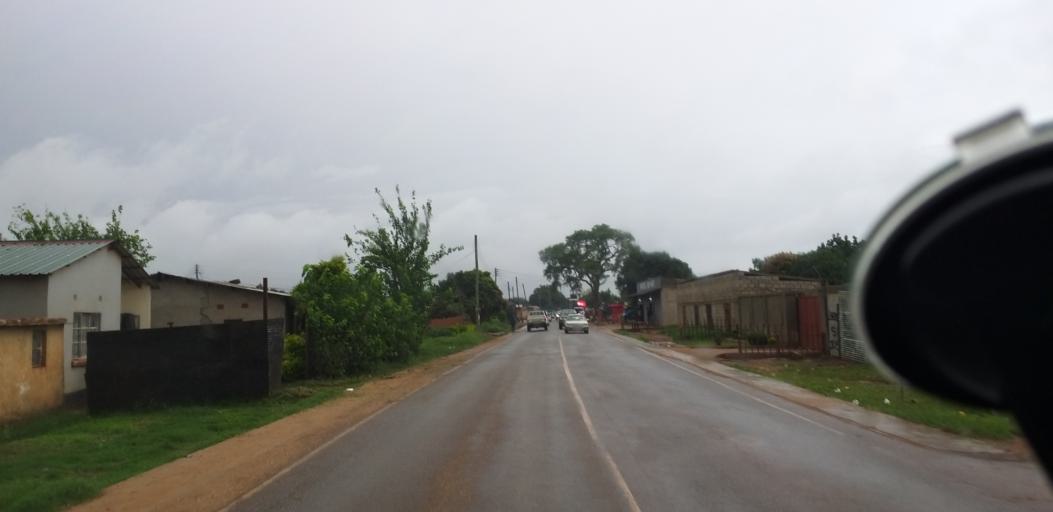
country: ZM
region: Lusaka
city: Lusaka
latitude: -15.5153
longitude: 28.2979
